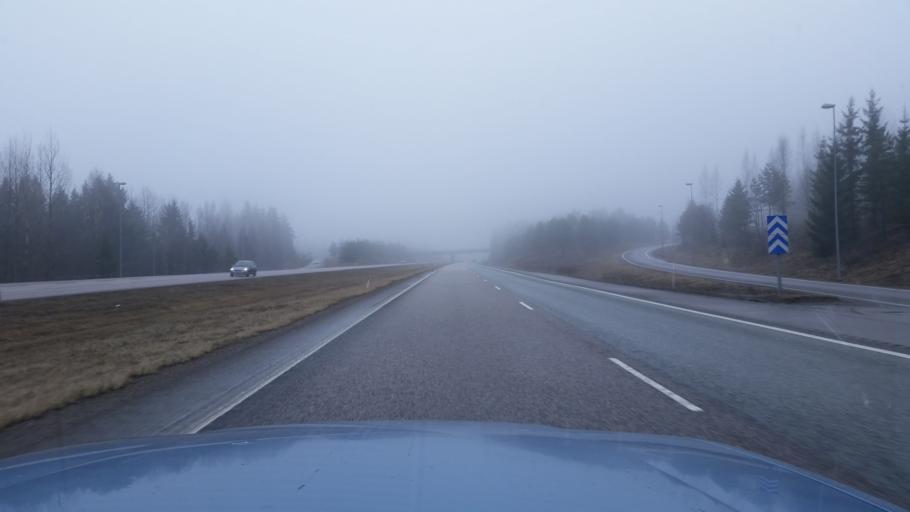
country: FI
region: Uusimaa
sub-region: Helsinki
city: Nurmijaervi
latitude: 60.4603
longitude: 24.8482
